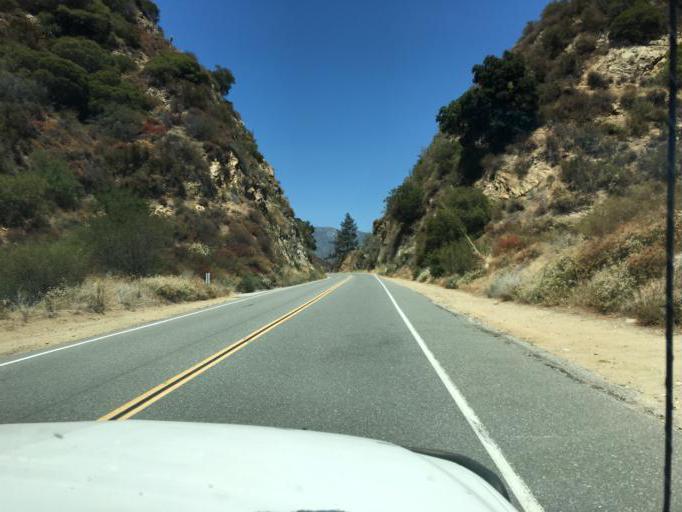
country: US
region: California
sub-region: Los Angeles County
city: Glendora
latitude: 34.2061
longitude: -117.8661
